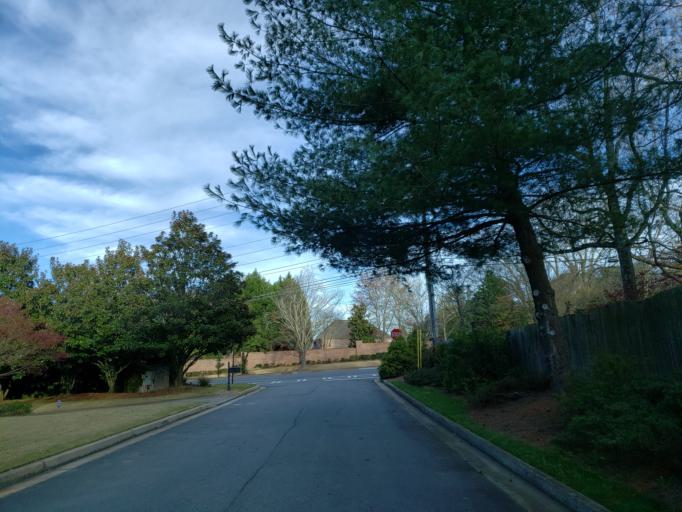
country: US
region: Georgia
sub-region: Cobb County
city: Vinings
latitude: 33.9282
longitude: -84.4616
